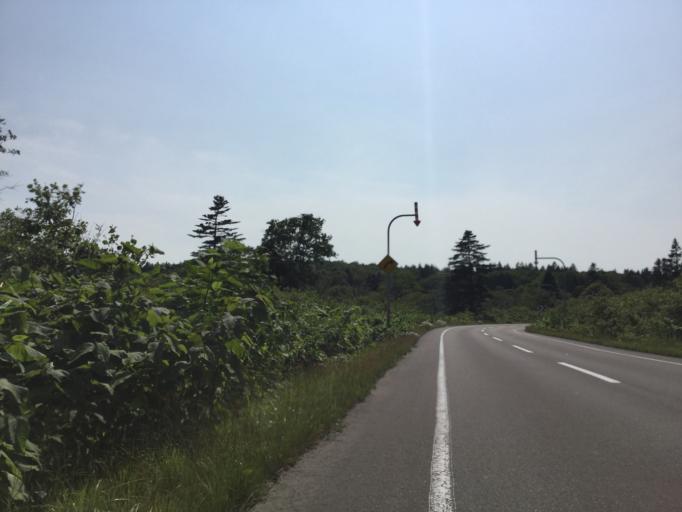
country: JP
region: Hokkaido
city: Makubetsu
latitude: 45.4064
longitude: 141.9939
